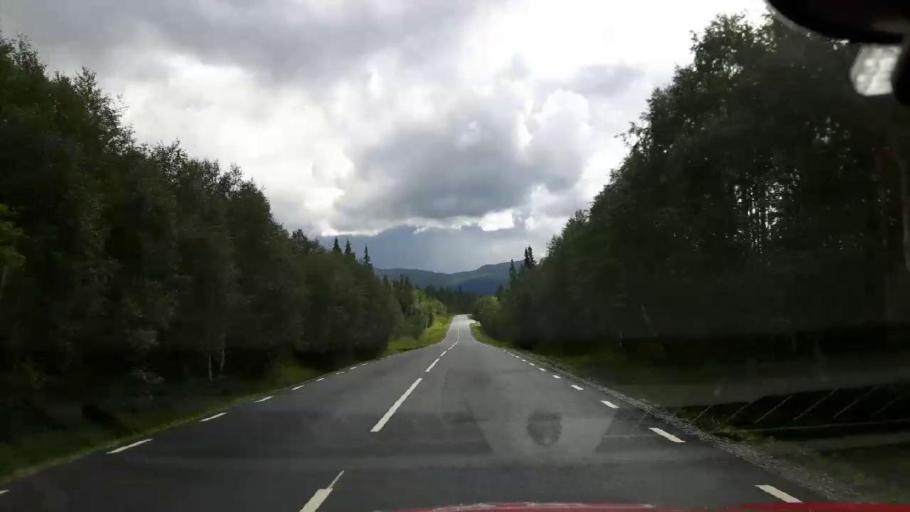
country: NO
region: Nord-Trondelag
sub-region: Royrvik
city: Royrvik
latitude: 64.8820
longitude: 14.2082
